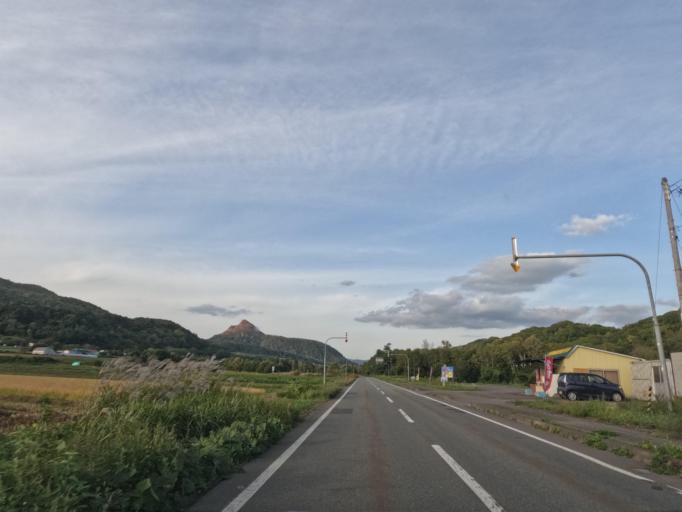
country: JP
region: Hokkaido
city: Date
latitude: 42.5120
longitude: 140.8632
